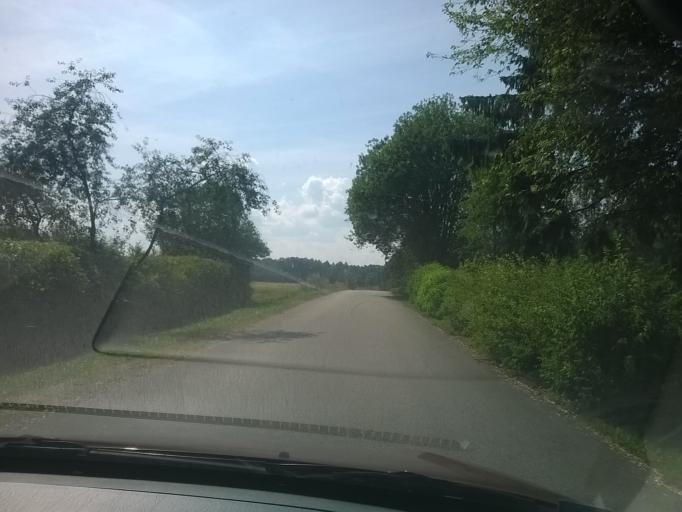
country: EE
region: Tartu
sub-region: Puhja vald
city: Puhja
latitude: 58.2314
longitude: 26.1371
